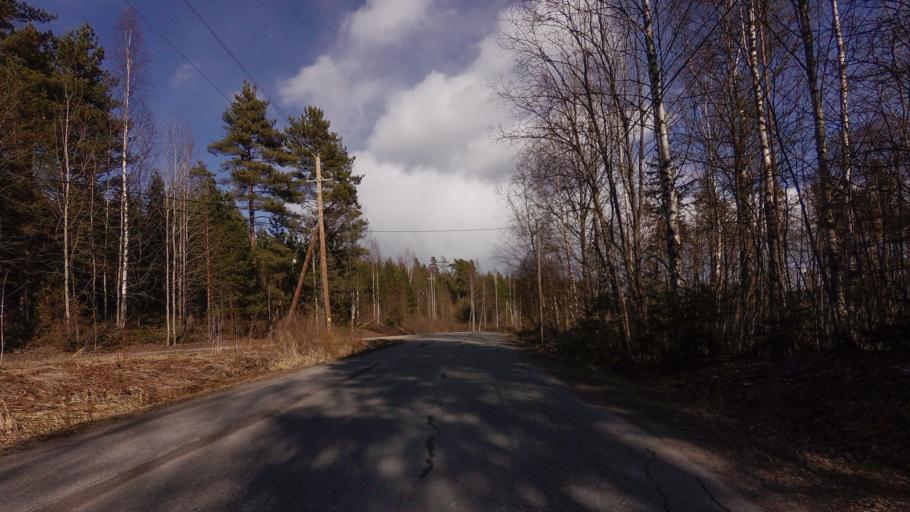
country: FI
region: Uusimaa
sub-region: Helsinki
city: Karjalohja
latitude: 60.2614
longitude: 23.7031
